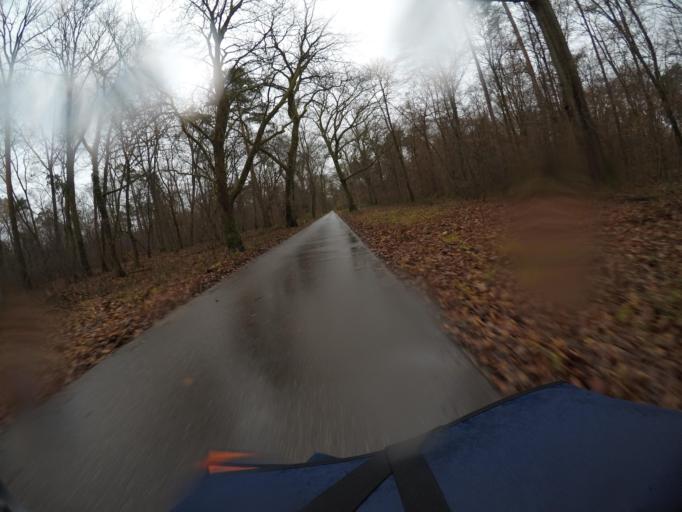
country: DE
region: Baden-Wuerttemberg
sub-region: Karlsruhe Region
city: Karlsruhe
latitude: 49.0289
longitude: 8.4156
